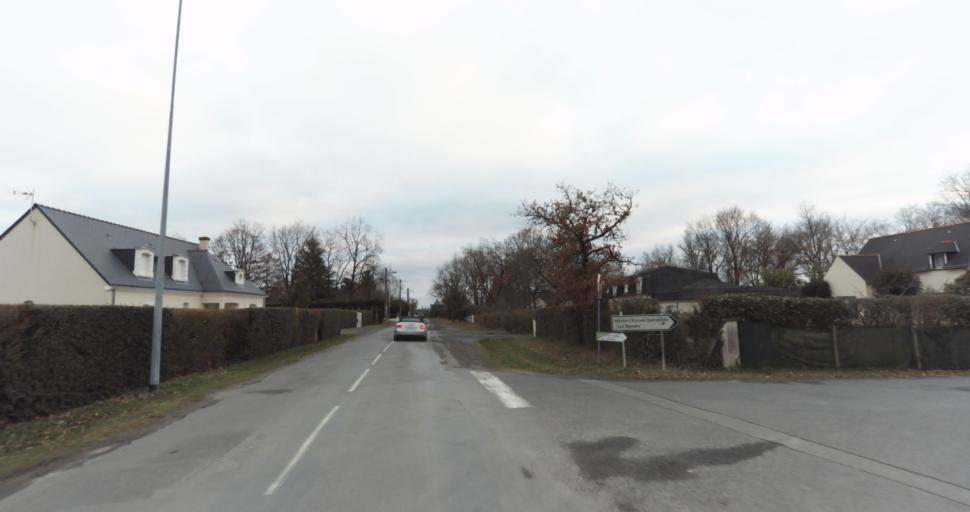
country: FR
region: Pays de la Loire
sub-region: Departement de Maine-et-Loire
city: Distre
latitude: 47.2515
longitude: -0.1118
